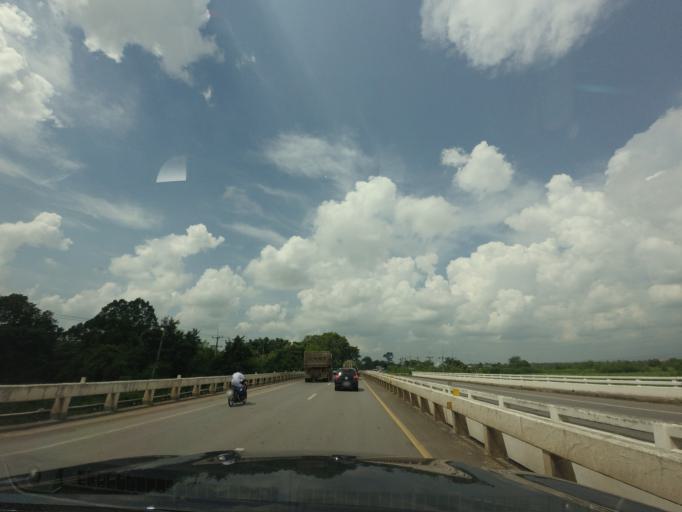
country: TH
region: Khon Kaen
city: Nong Ruea
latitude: 16.4888
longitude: 102.4193
